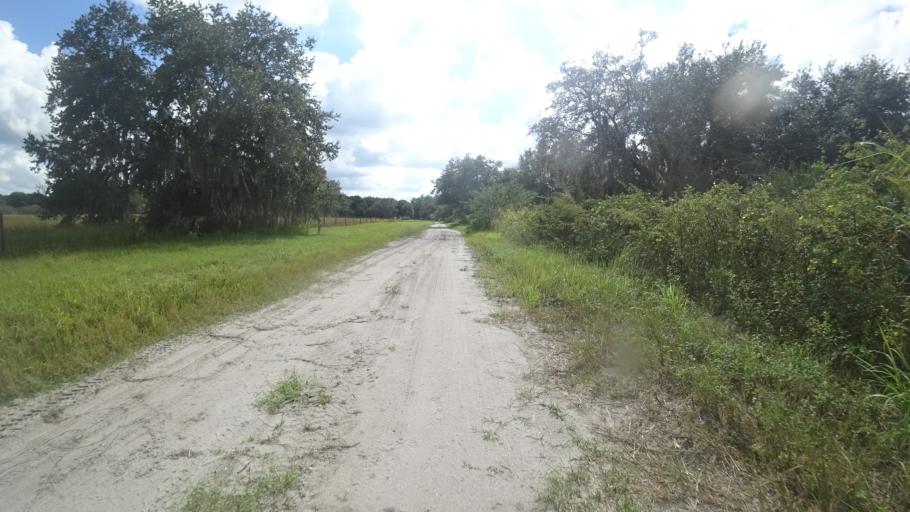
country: US
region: Florida
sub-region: Hillsborough County
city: Wimauma
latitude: 27.5678
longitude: -82.2705
